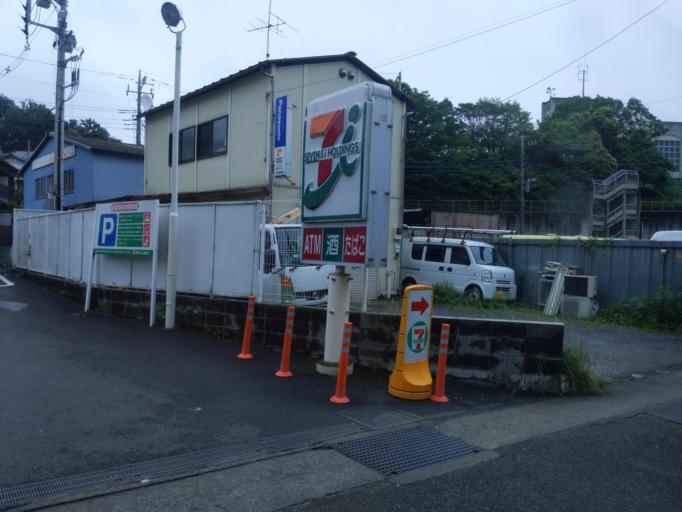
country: JP
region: Tokyo
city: Chofugaoka
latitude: 35.6041
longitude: 139.5681
